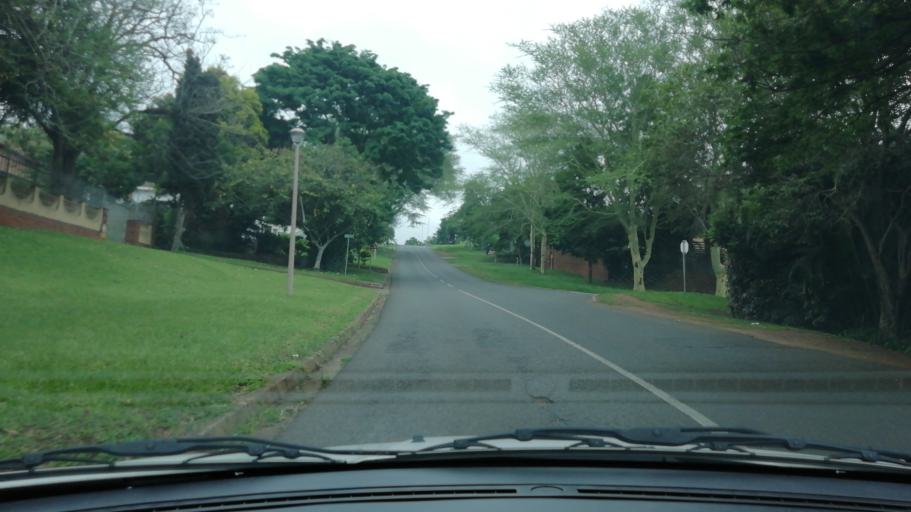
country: ZA
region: KwaZulu-Natal
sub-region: uThungulu District Municipality
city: Empangeni
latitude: -28.7524
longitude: 31.8876
